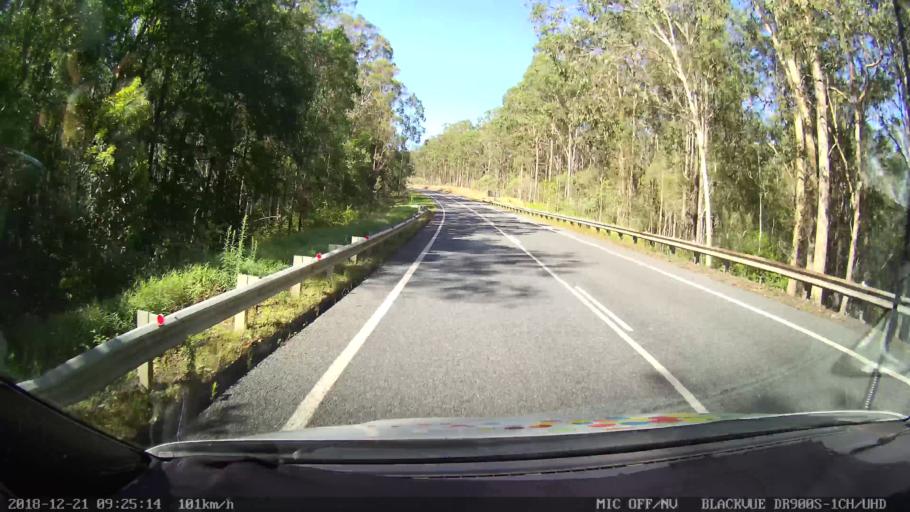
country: AU
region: New South Wales
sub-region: Clarence Valley
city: Maclean
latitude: -29.3768
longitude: 153.0094
